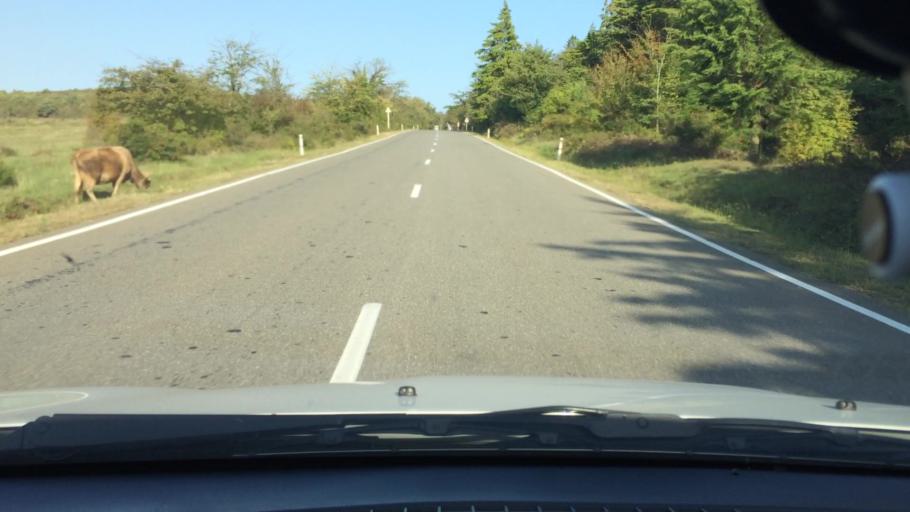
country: GE
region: Imereti
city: Kutaisi
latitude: 42.2427
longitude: 42.7625
